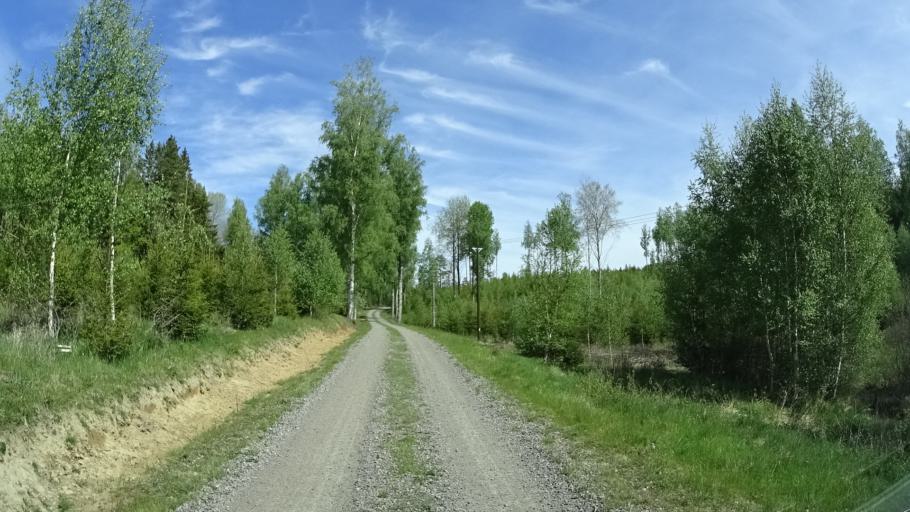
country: SE
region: OEstergoetland
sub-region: Finspangs Kommun
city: Finspang
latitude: 58.8017
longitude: 15.8384
